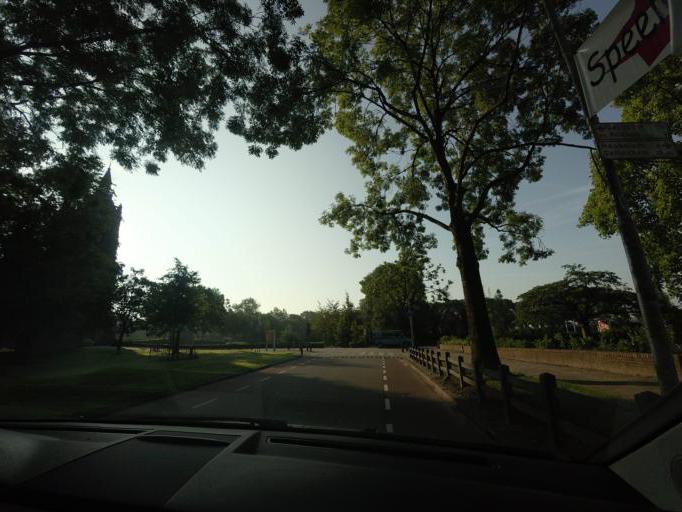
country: NL
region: South Holland
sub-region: Gemeente Leerdam
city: Leerdam
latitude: 51.8810
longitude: 5.1100
